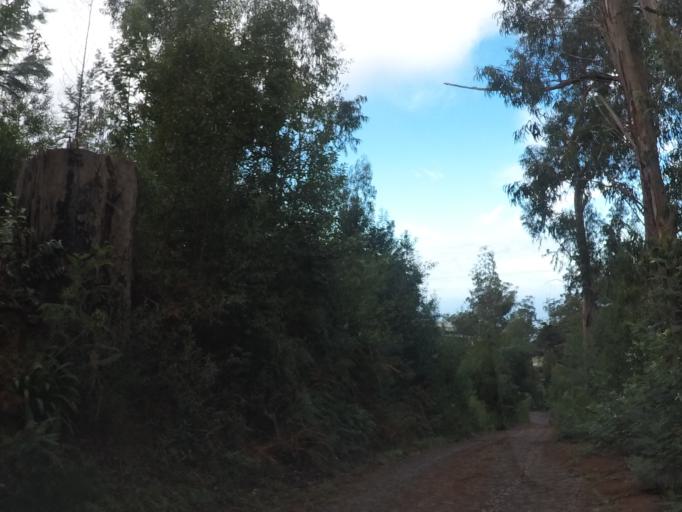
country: PT
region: Madeira
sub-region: Funchal
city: Nossa Senhora do Monte
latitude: 32.6737
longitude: -16.8819
